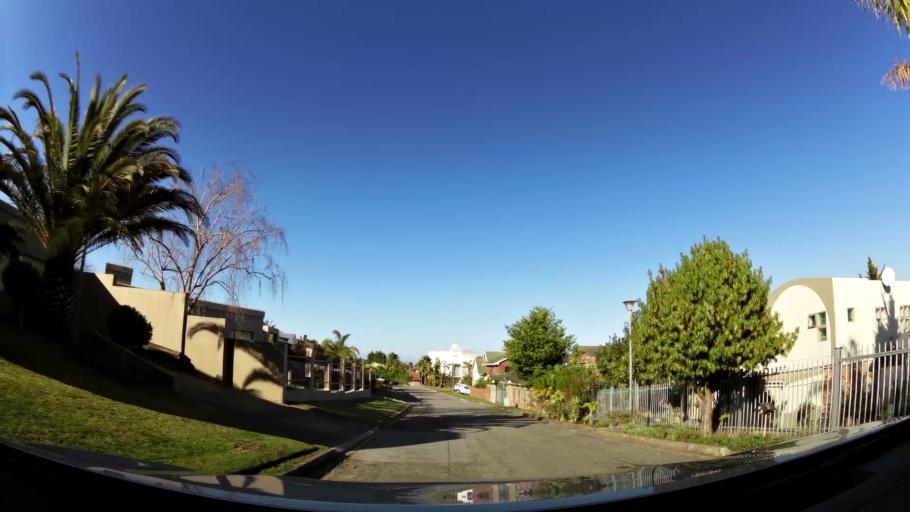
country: ZA
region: Western Cape
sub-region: Eden District Municipality
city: George
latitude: -33.9687
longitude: 22.4376
